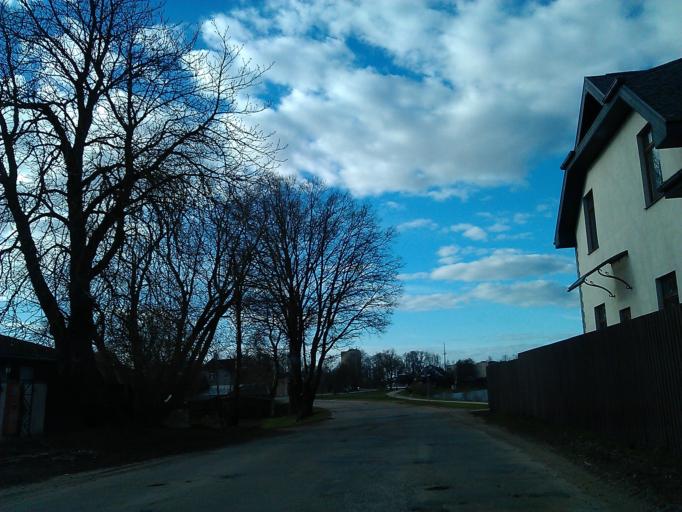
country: LV
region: Adazi
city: Adazi
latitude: 57.0740
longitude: 24.3313
